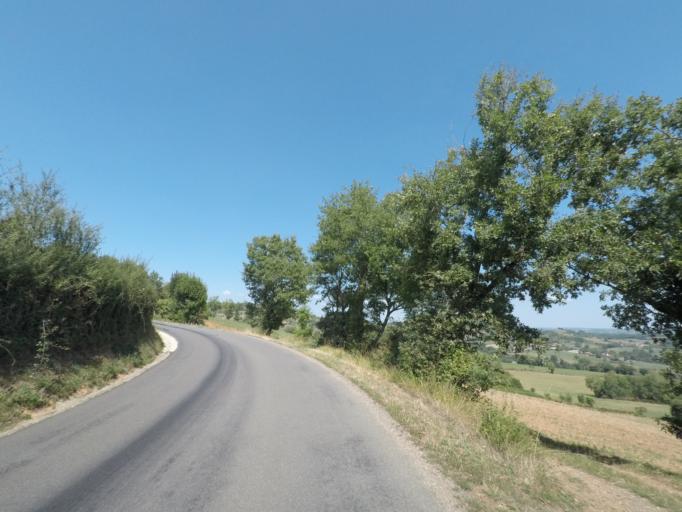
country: FR
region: Midi-Pyrenees
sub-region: Departement de l'Aveyron
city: Livinhac-le-Haut
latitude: 44.6160
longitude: 2.2112
